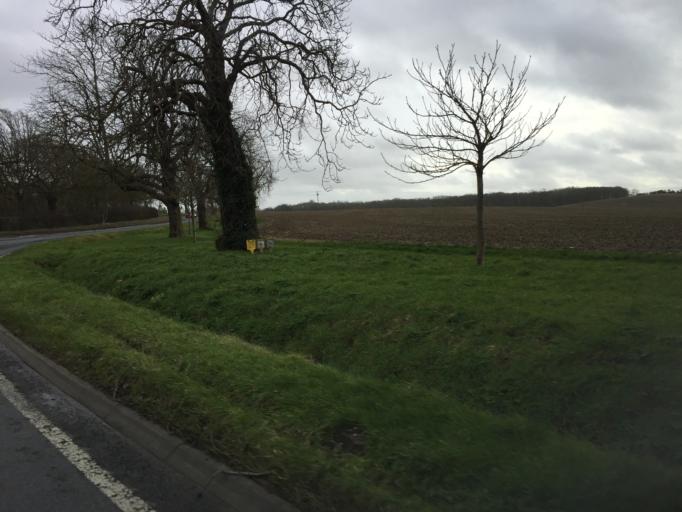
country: GB
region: England
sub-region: Gloucestershire
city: Lechlade
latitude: 51.6768
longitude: -1.6593
